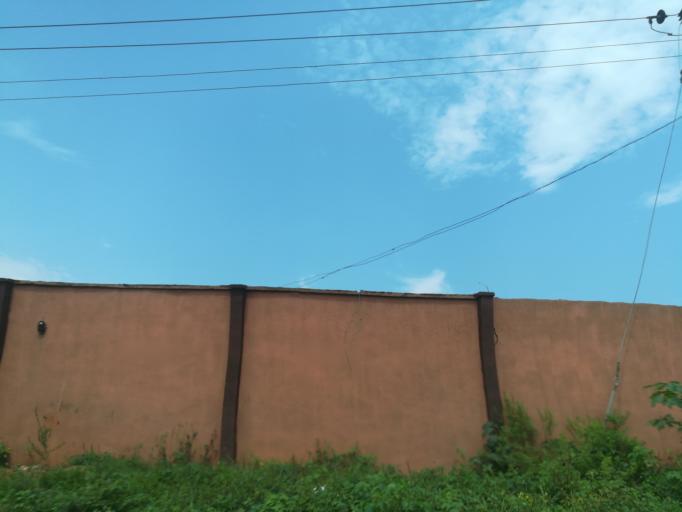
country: NG
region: Lagos
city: Ikorodu
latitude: 6.5832
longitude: 3.6259
